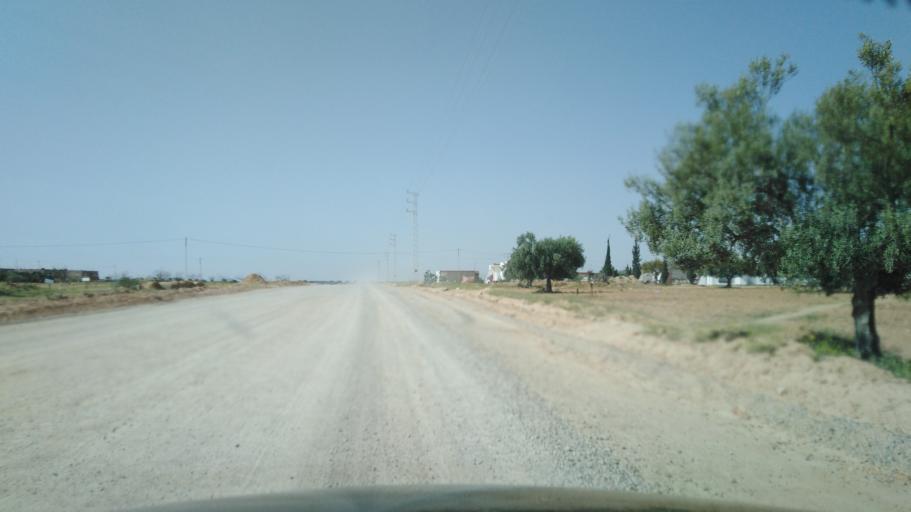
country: TN
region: Safaqis
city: Sfax
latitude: 34.7227
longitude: 10.5102
